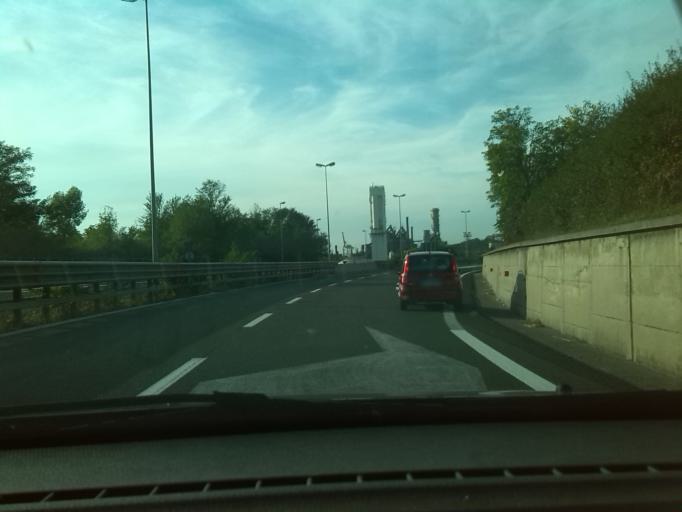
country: IT
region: Friuli Venezia Giulia
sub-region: Provincia di Trieste
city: Muggia
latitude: 45.6161
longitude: 13.7886
